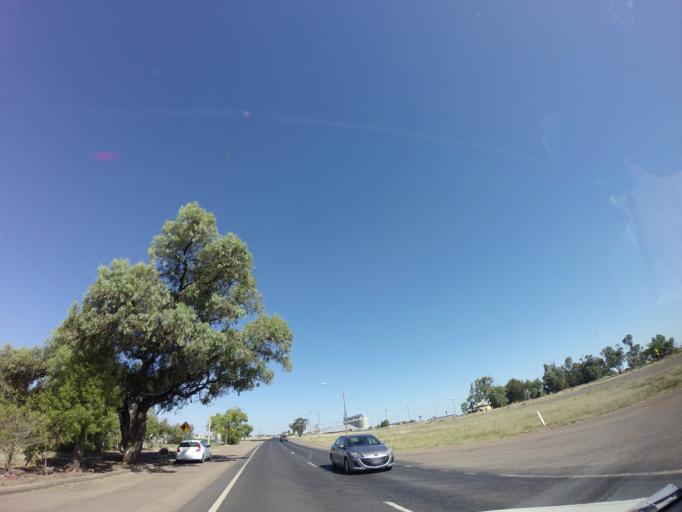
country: AU
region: New South Wales
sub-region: Bogan
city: Nyngan
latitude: -31.8378
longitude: 147.7178
